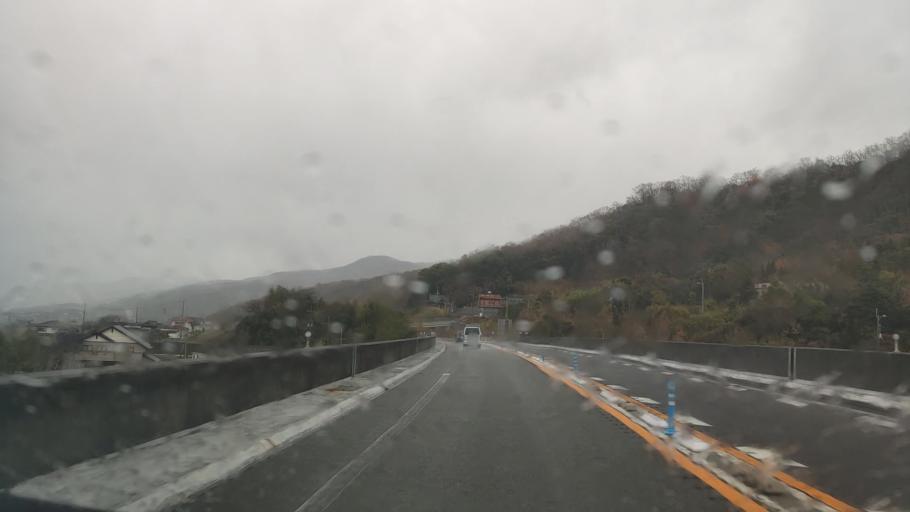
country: JP
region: Tokushima
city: Kamojimacho-jogejima
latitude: 34.1082
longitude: 134.2888
